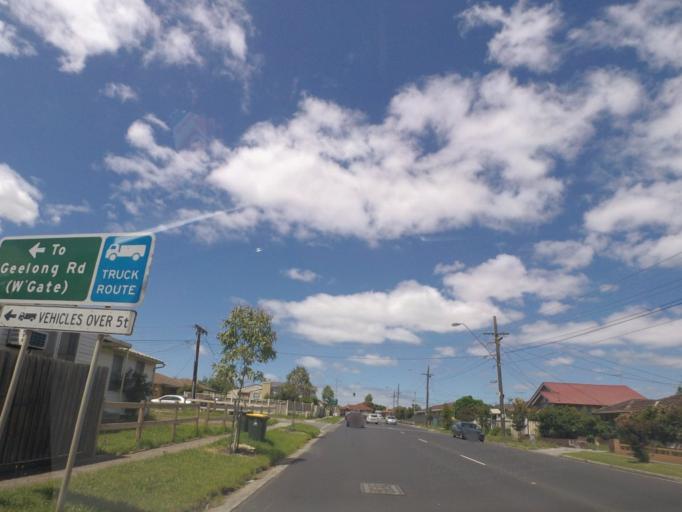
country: AU
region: Victoria
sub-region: Brimbank
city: Sunshine West
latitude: -37.7943
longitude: 144.8266
